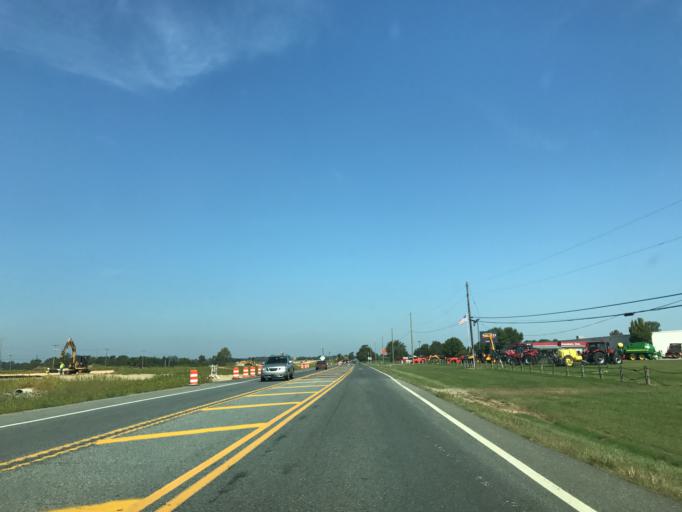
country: US
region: Delaware
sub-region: New Castle County
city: Middletown
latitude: 39.4237
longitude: -75.7625
